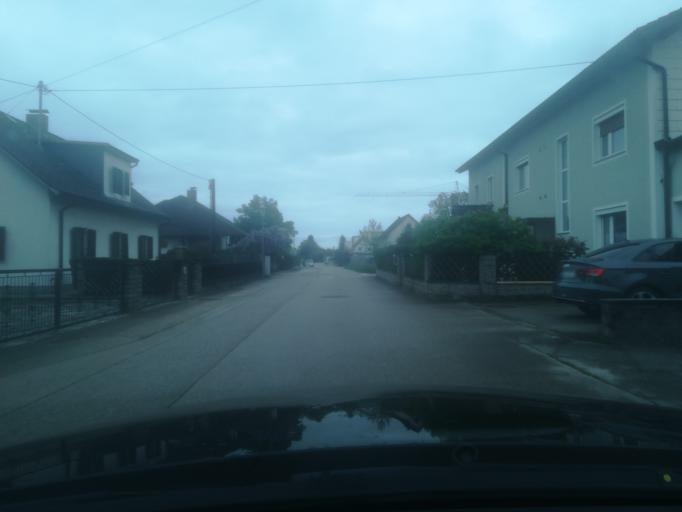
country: AT
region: Upper Austria
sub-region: Wels-Land
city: Marchtrenk
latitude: 48.1957
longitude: 14.1196
